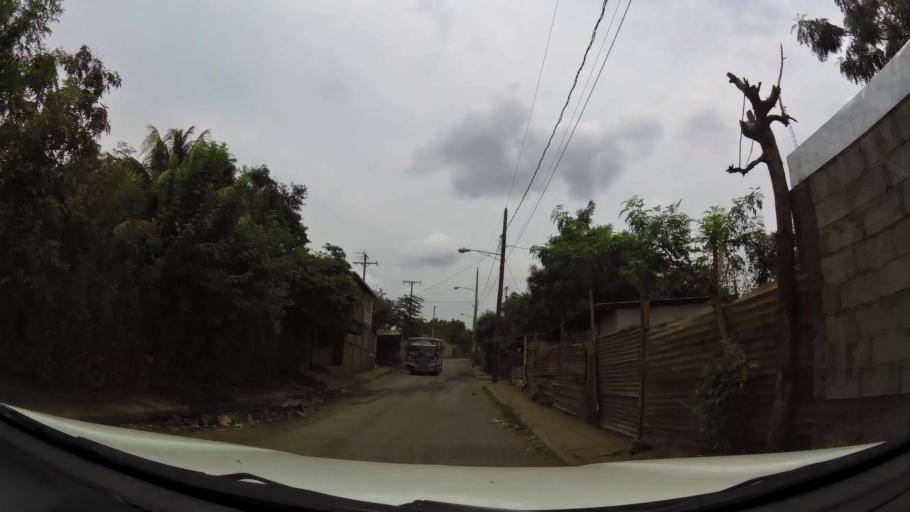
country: NI
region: Managua
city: Managua
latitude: 12.1137
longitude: -86.2171
